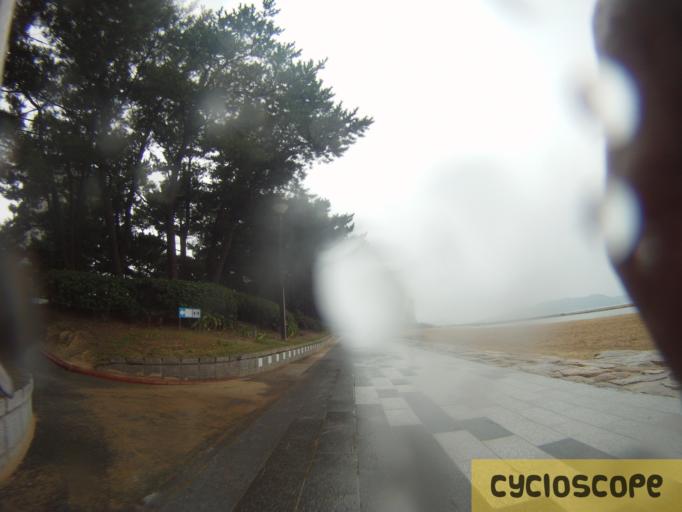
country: JP
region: Fukuoka
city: Fukuoka-shi
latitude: 33.5938
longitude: 130.3460
